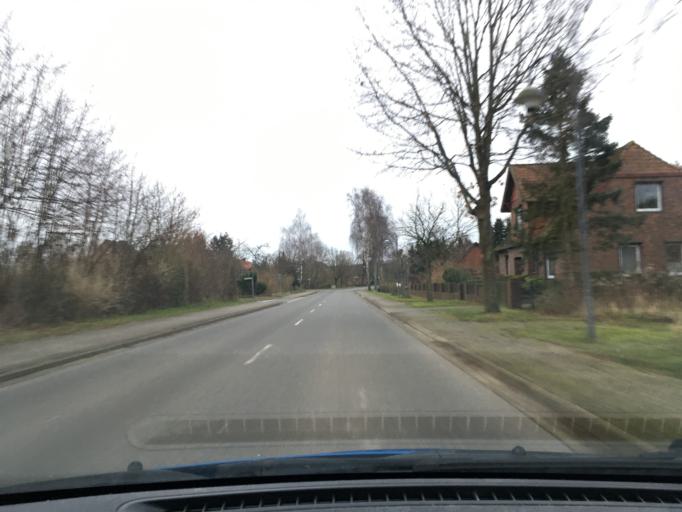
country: DE
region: Lower Saxony
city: Neu Darchau
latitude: 53.2327
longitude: 10.8726
